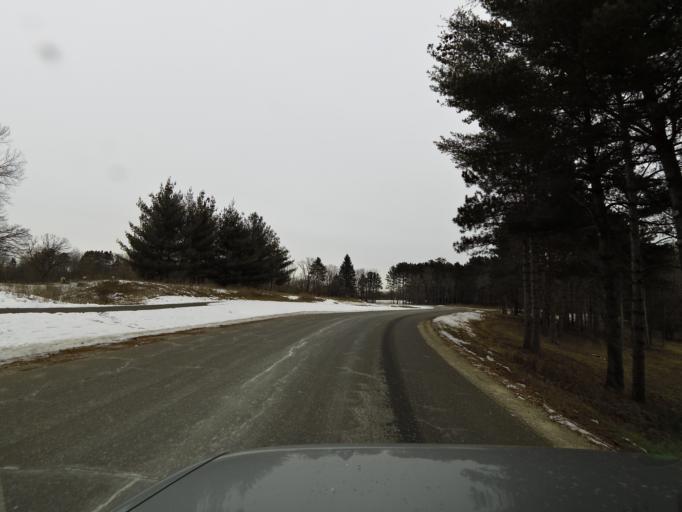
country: US
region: Minnesota
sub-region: Washington County
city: Lake Elmo
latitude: 44.9746
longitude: -92.9046
